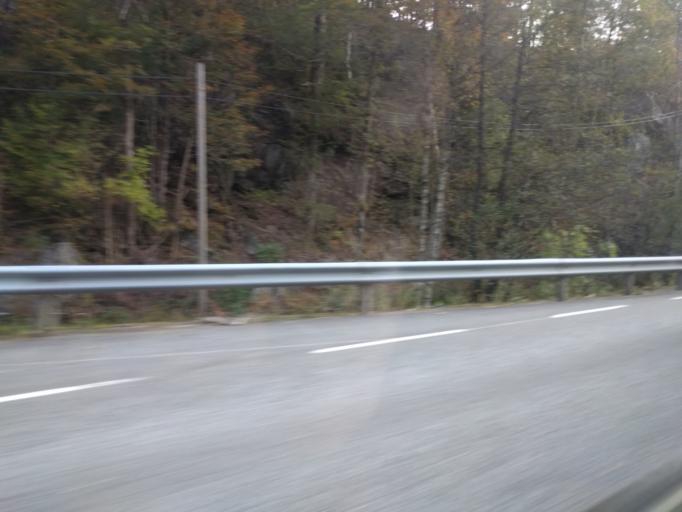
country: NO
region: Vest-Agder
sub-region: Kristiansand
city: Strai
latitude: 58.2460
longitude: 7.8740
